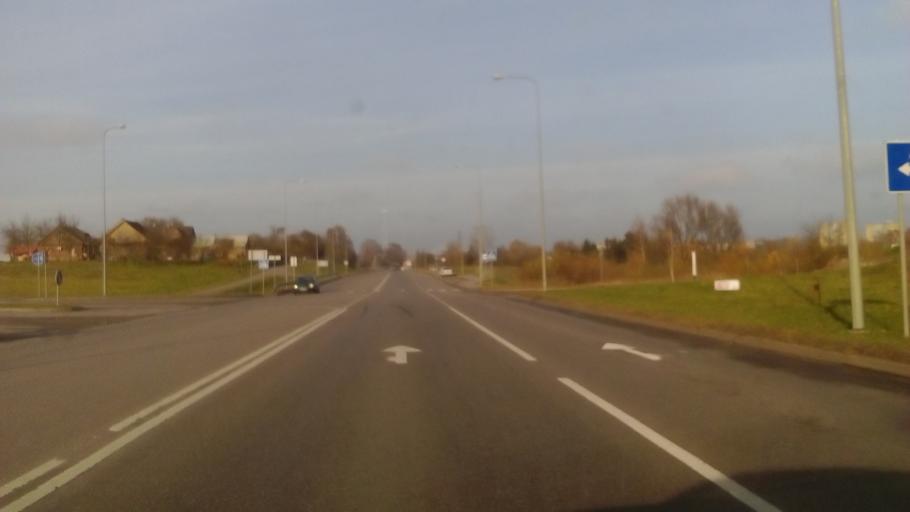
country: LT
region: Alytaus apskritis
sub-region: Alytus
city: Alytus
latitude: 54.4045
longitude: 24.0027
